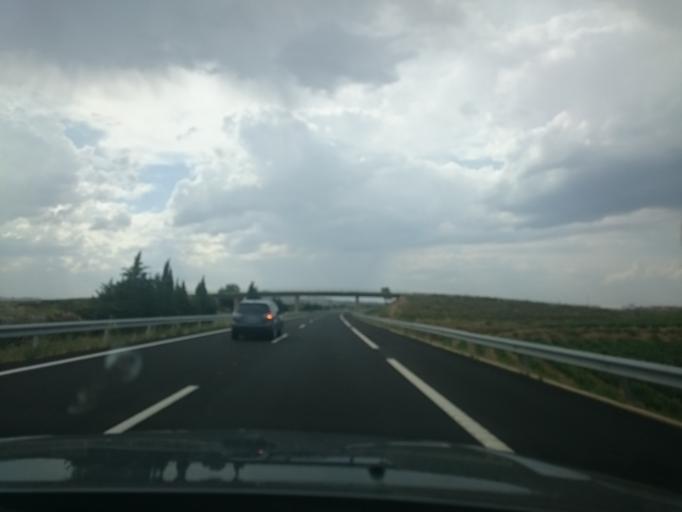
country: ES
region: La Rioja
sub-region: Provincia de La Rioja
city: Aldeanueva de Ebro
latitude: 42.2128
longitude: -1.8817
